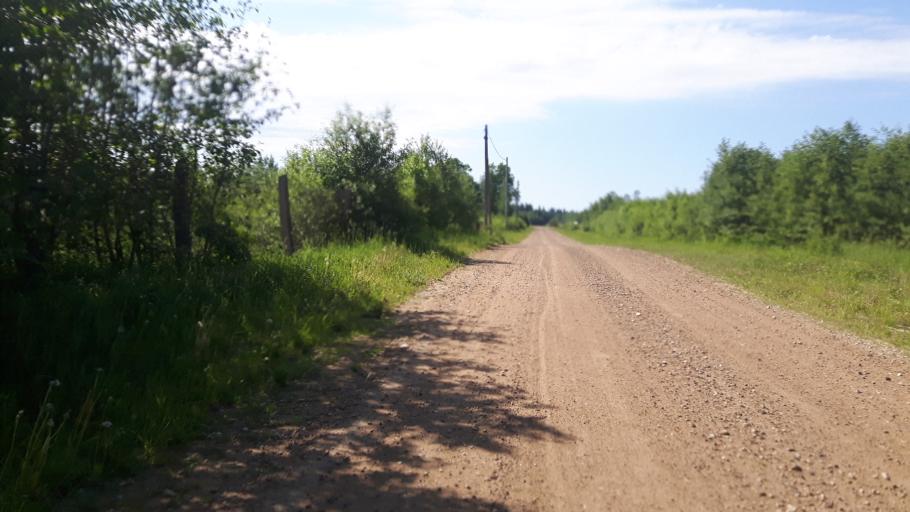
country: EE
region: Paernumaa
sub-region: Vaendra vald (alev)
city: Vandra
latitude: 58.6750
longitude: 25.0305
